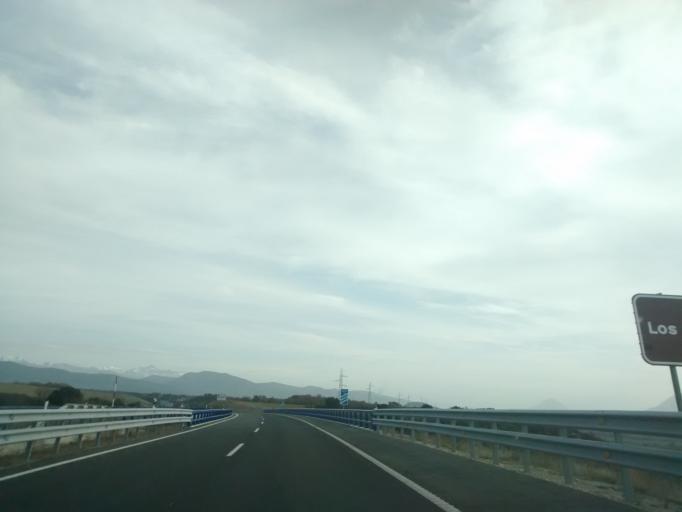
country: ES
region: Aragon
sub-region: Provincia de Zaragoza
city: Mianos
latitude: 42.6099
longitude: -0.9423
